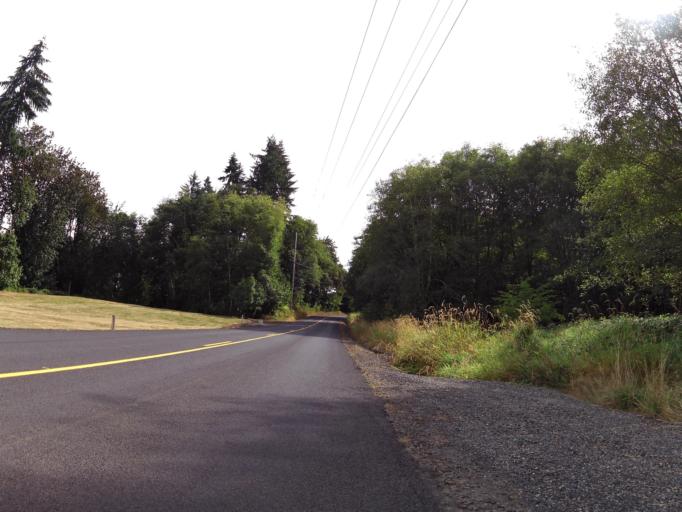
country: US
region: Washington
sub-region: Cowlitz County
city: Castle Rock
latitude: 46.3184
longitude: -122.9249
